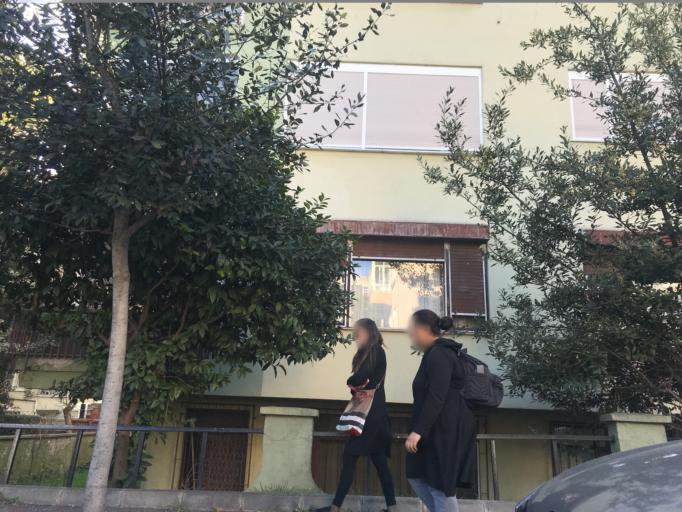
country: TR
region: Istanbul
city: Bahcelievler
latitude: 40.9611
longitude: 28.8336
